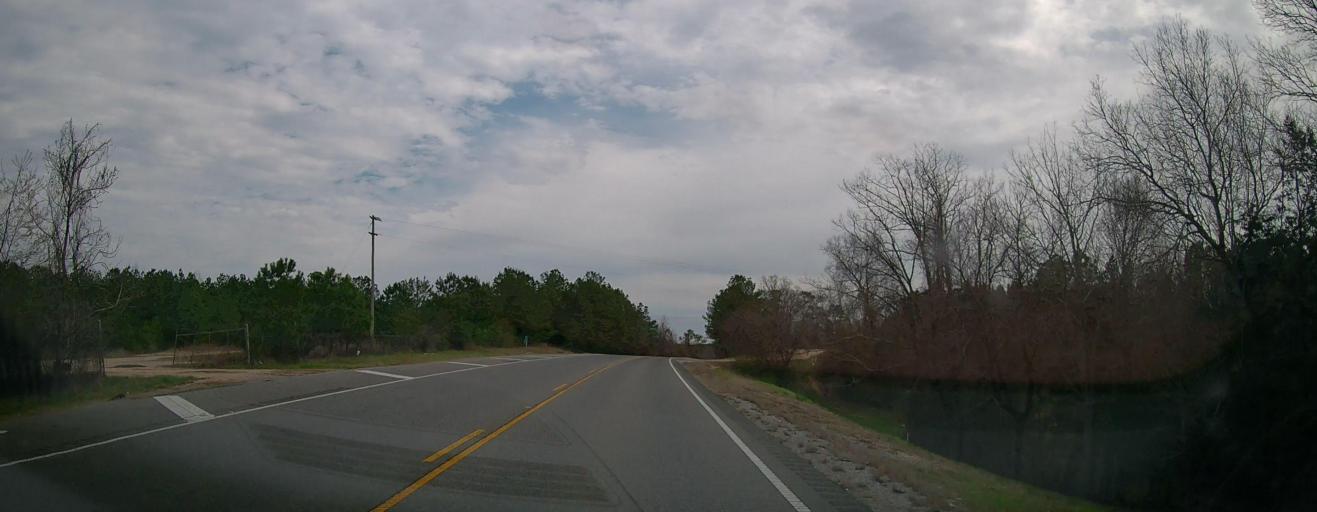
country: US
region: Alabama
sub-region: Marion County
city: Guin
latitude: 34.0294
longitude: -87.9427
